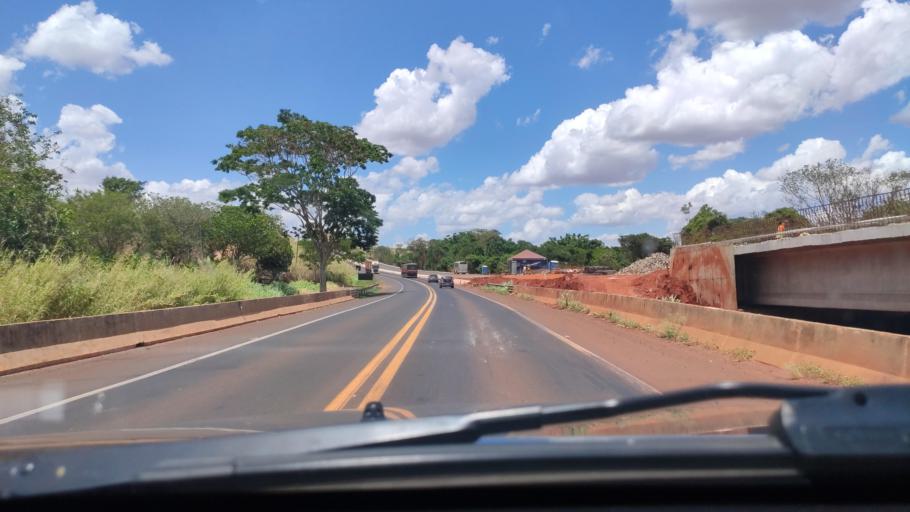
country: BR
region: Sao Paulo
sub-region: Jau
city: Jau
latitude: -22.2334
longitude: -48.5337
